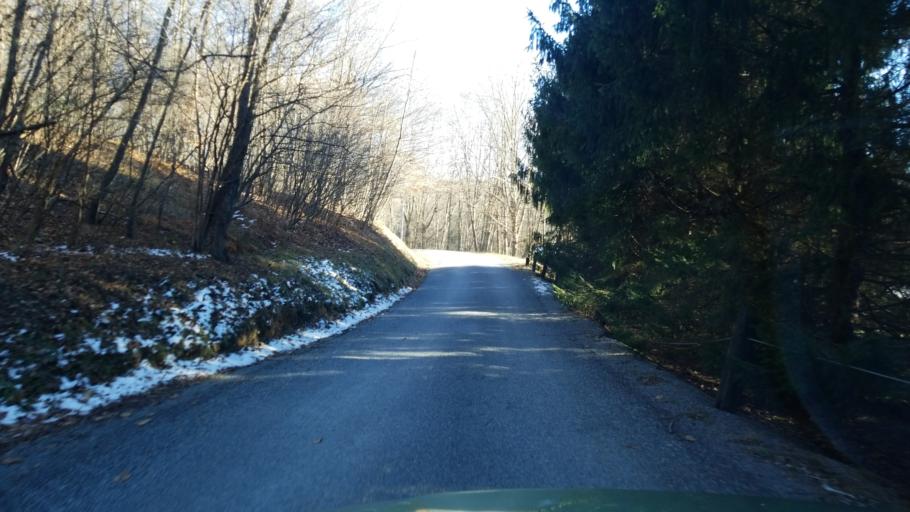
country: US
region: Pennsylvania
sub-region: Jefferson County
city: Brockway
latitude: 41.2795
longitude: -78.8244
